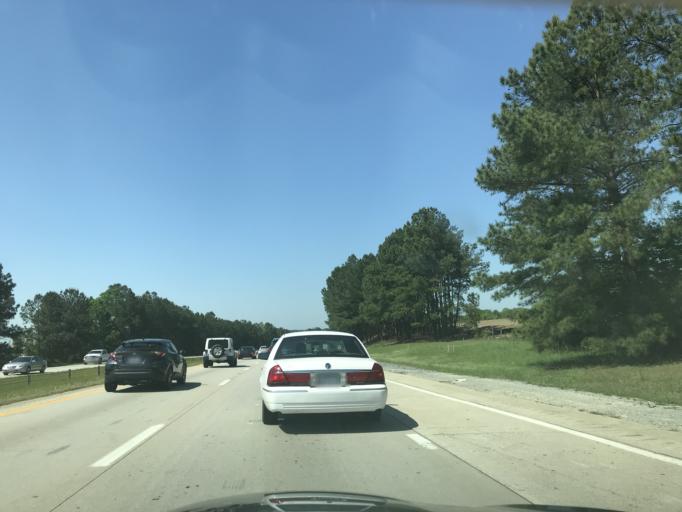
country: US
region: North Carolina
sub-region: Wake County
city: Garner
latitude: 35.6130
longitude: -78.5666
